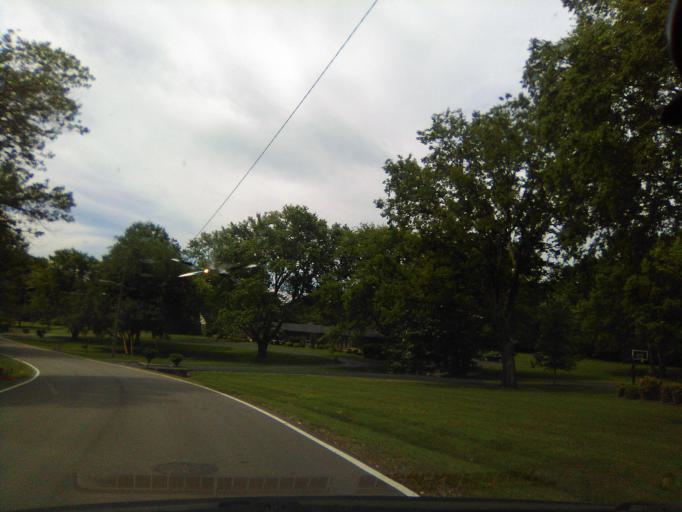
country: US
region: Tennessee
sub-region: Davidson County
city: Belle Meade
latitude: 36.0996
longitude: -86.8798
